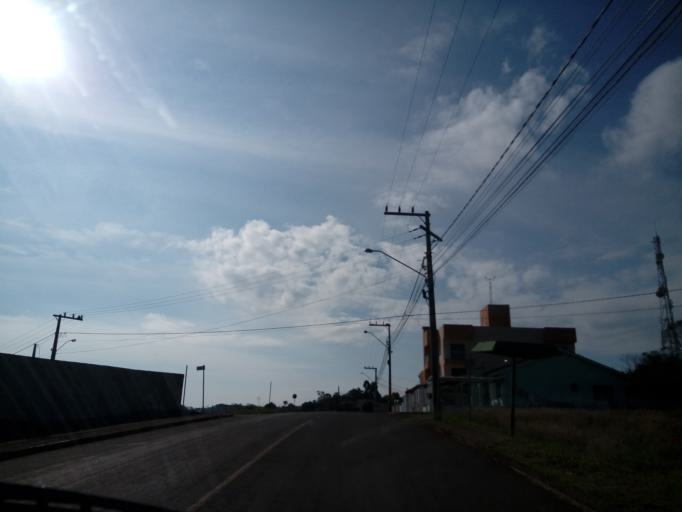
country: BR
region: Santa Catarina
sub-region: Chapeco
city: Chapeco
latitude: -27.1053
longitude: -52.5841
